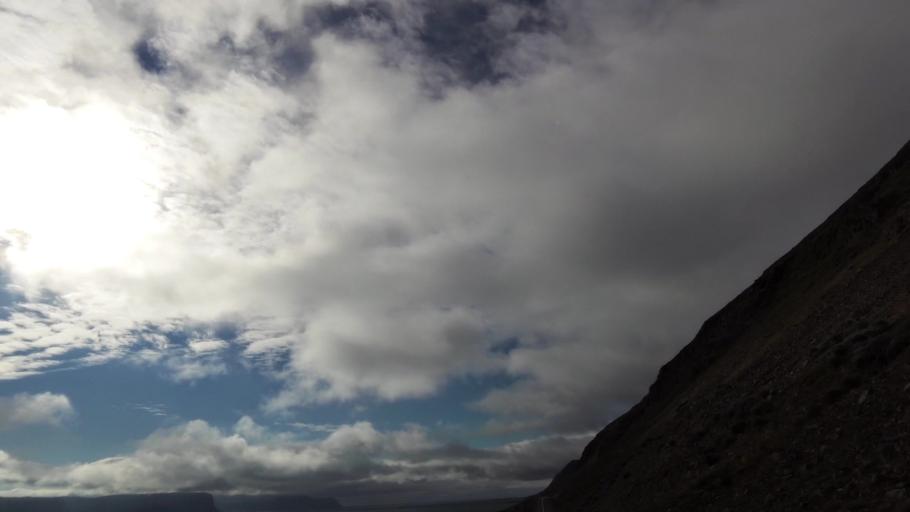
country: IS
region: West
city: Olafsvik
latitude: 65.5636
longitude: -23.9161
